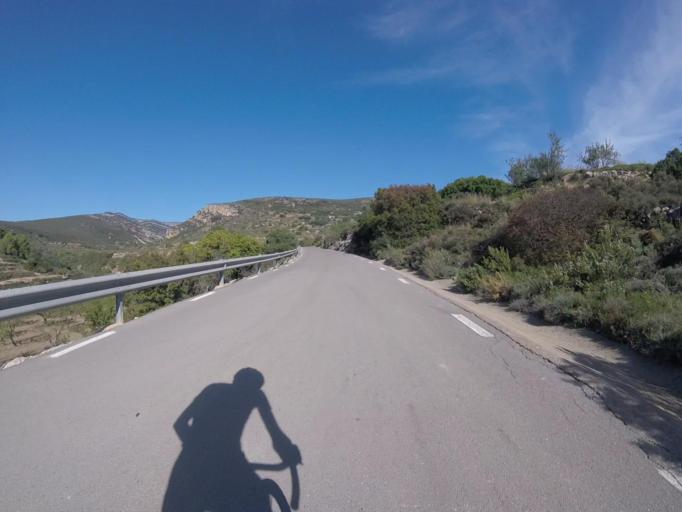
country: ES
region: Valencia
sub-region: Provincia de Castello
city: Sarratella
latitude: 40.2741
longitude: 0.0364
